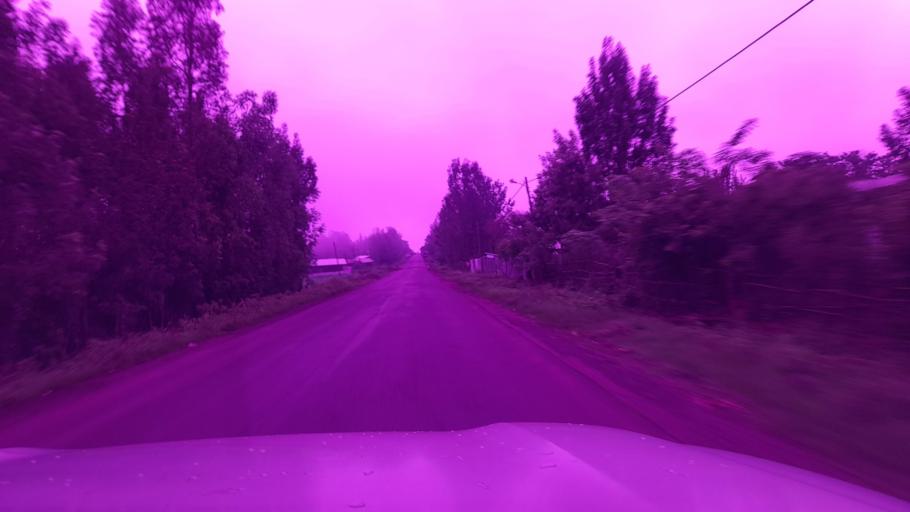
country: ET
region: Oromiya
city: Waliso
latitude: 8.1743
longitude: 37.5673
